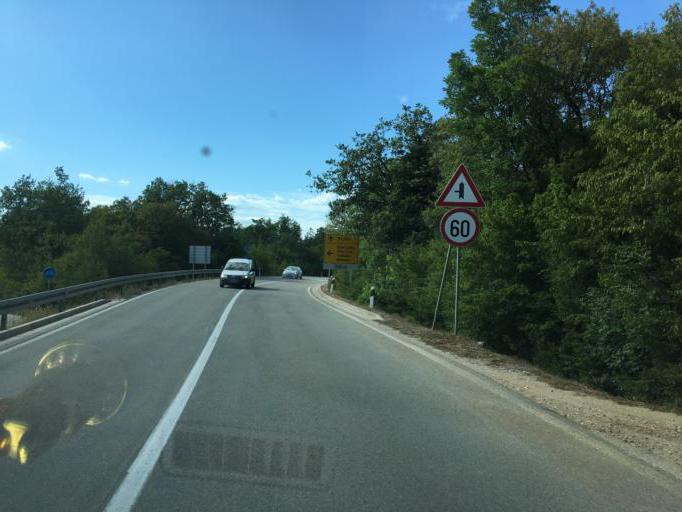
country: HR
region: Primorsko-Goranska
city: Njivice
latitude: 45.0920
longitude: 14.5384
